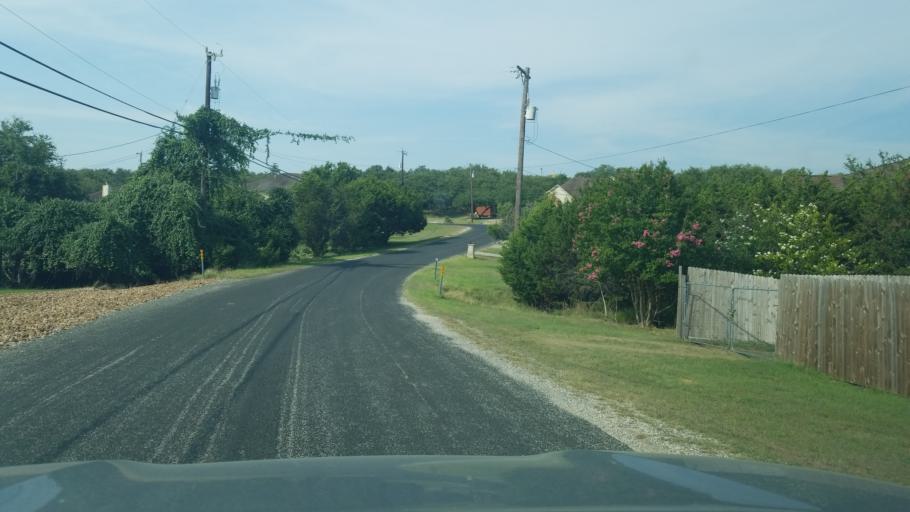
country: US
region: Texas
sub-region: Bexar County
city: Timberwood Park
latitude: 29.6926
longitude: -98.4956
